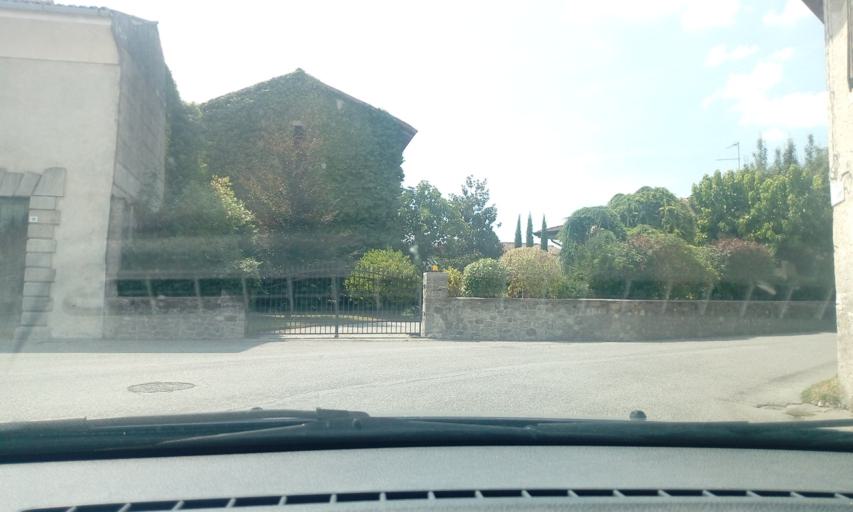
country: IT
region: Friuli Venezia Giulia
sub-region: Provincia di Udine
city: Povoletto
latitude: 46.1416
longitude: 13.3070
